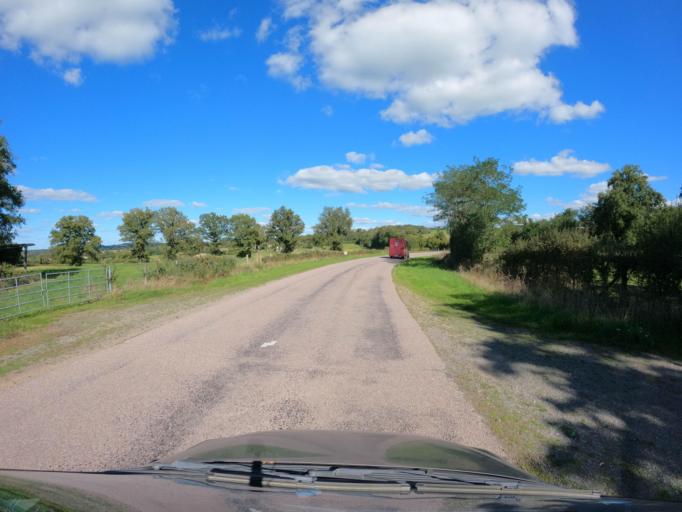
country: FR
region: Auvergne
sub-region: Departement de l'Allier
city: Buxieres-les-Mines
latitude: 46.4044
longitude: 3.0155
